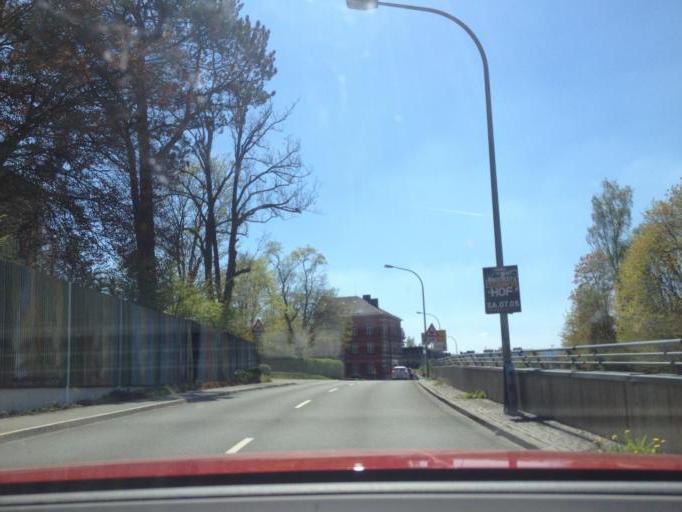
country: DE
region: Bavaria
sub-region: Upper Franconia
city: Schwarzenbach an der Saale
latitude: 50.2226
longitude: 11.9376
